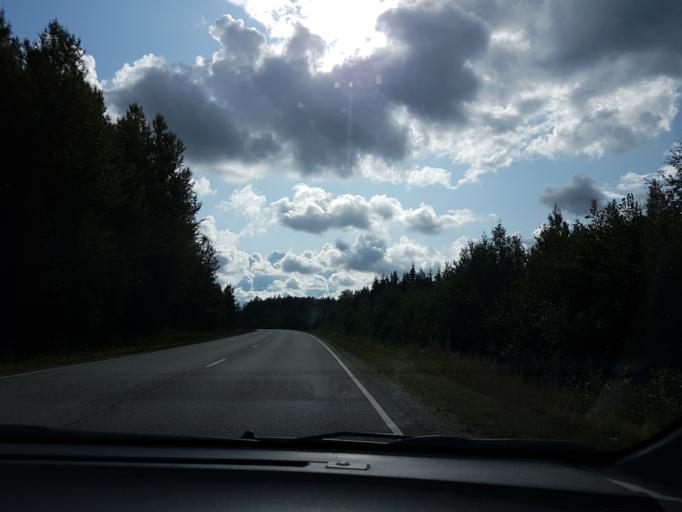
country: FI
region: Uusimaa
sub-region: Helsinki
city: Nickby
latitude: 60.4714
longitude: 25.2403
